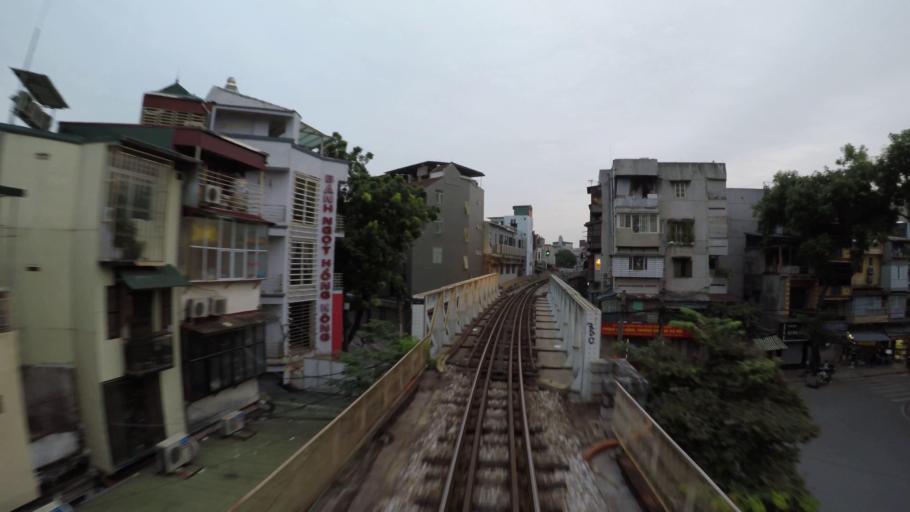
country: VN
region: Ha Noi
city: Hoan Kiem
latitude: 21.0449
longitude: 105.8622
